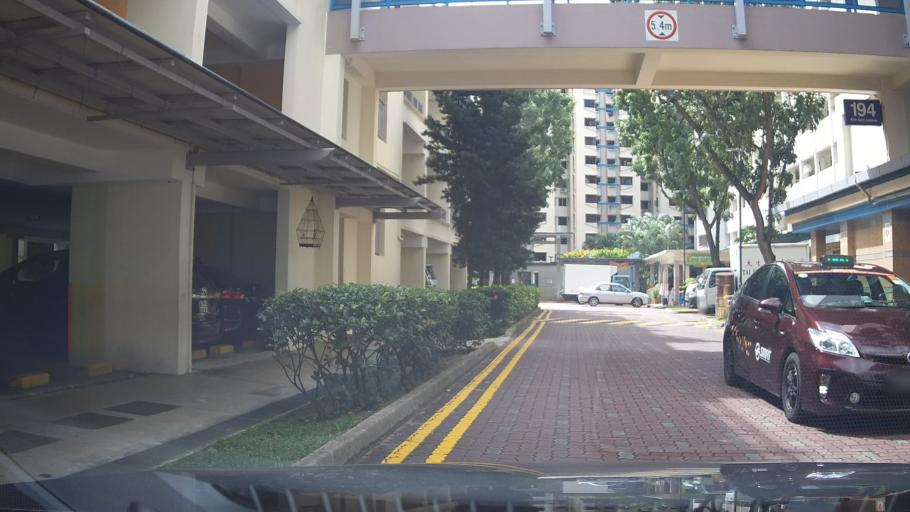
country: SG
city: Singapore
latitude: 1.3312
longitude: 103.8585
